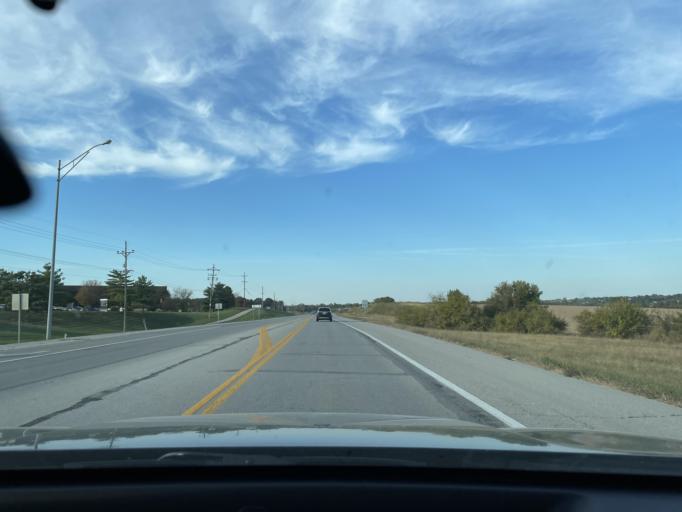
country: US
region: Missouri
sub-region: Buchanan County
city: Saint Joseph
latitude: 39.7708
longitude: -94.7683
